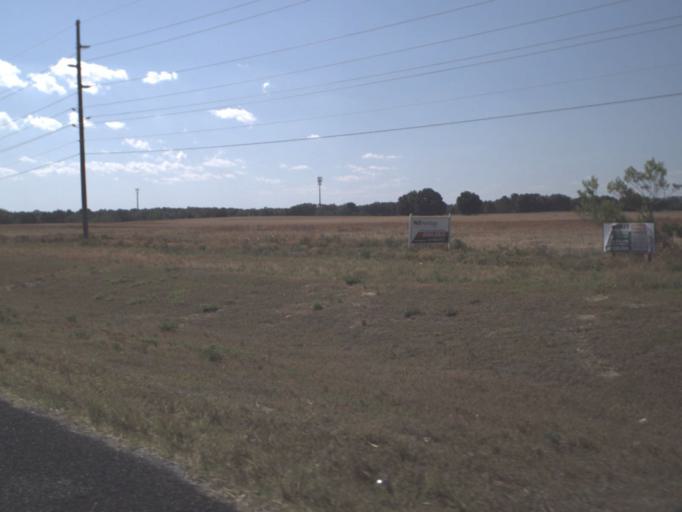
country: US
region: Florida
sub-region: Marion County
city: Ocala
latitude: 29.1864
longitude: -82.2206
